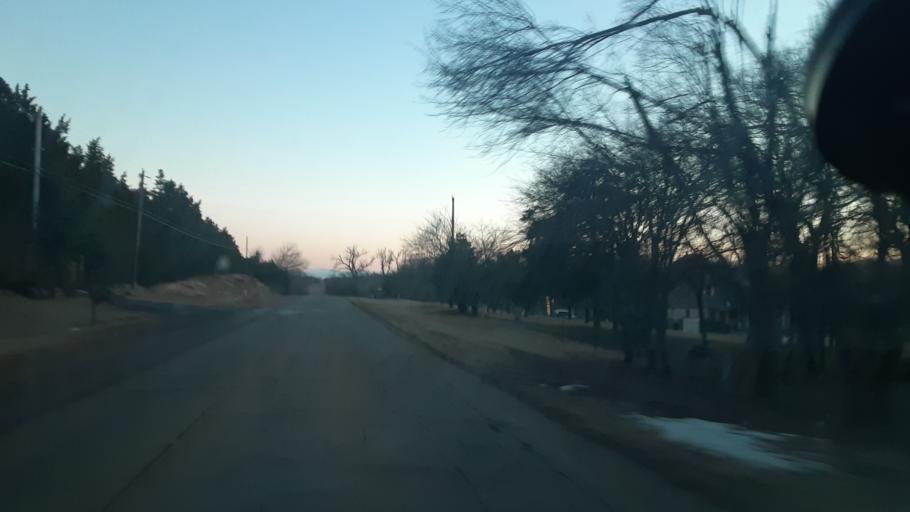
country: US
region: Oklahoma
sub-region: Oklahoma County
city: Edmond
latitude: 35.7212
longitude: -97.4252
